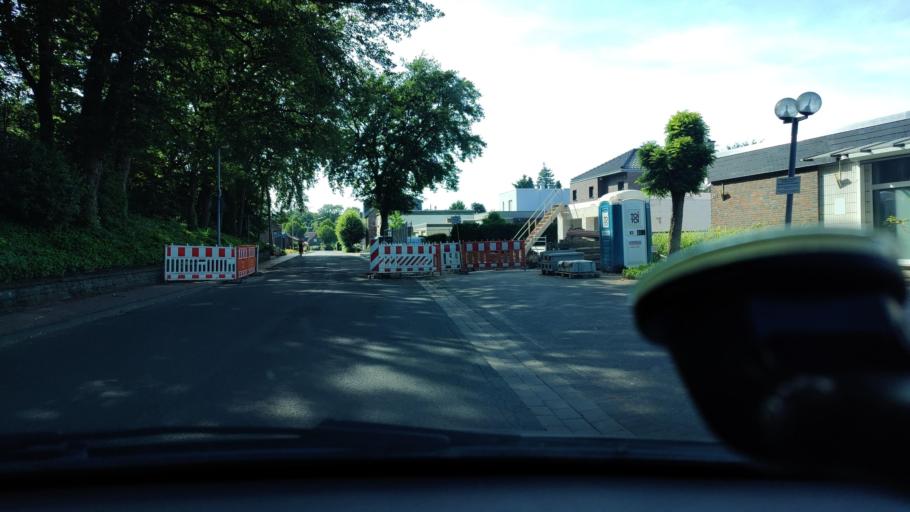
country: DE
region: North Rhine-Westphalia
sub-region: Regierungsbezirk Dusseldorf
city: Kamp-Lintfort
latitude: 51.4988
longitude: 6.5033
